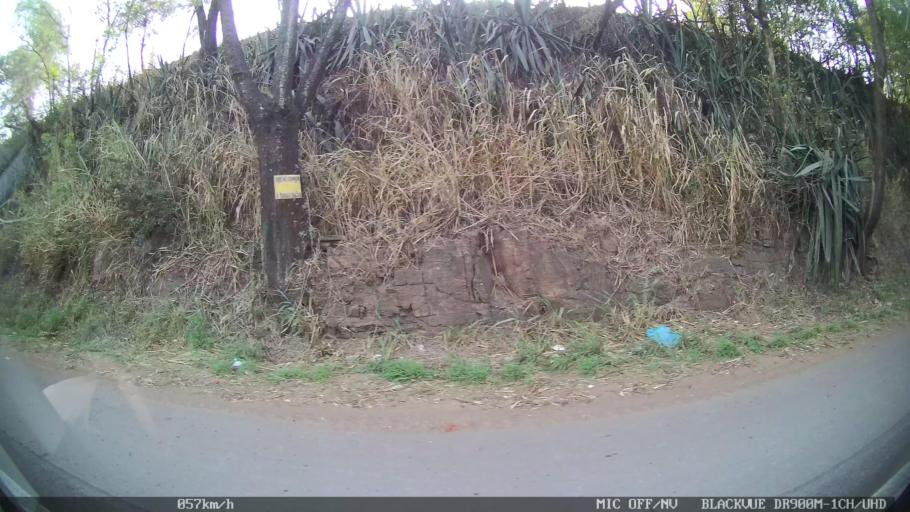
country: BR
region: Sao Paulo
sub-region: Piracicaba
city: Piracicaba
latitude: -22.6880
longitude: -47.6686
